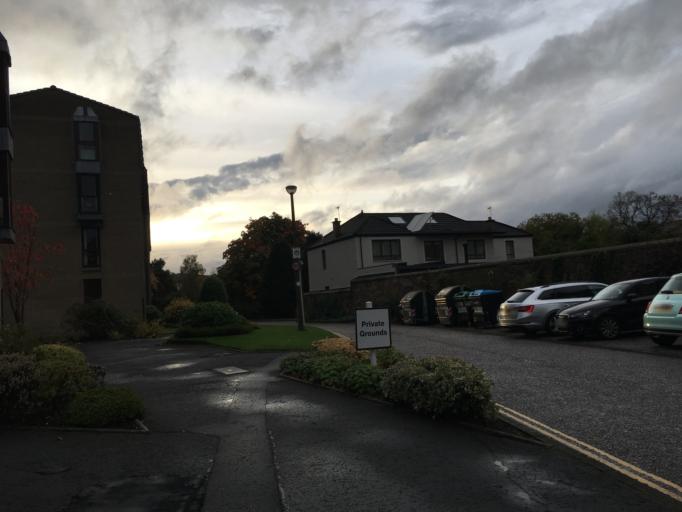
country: GB
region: Scotland
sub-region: Edinburgh
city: Edinburgh
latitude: 55.9251
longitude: -3.2112
